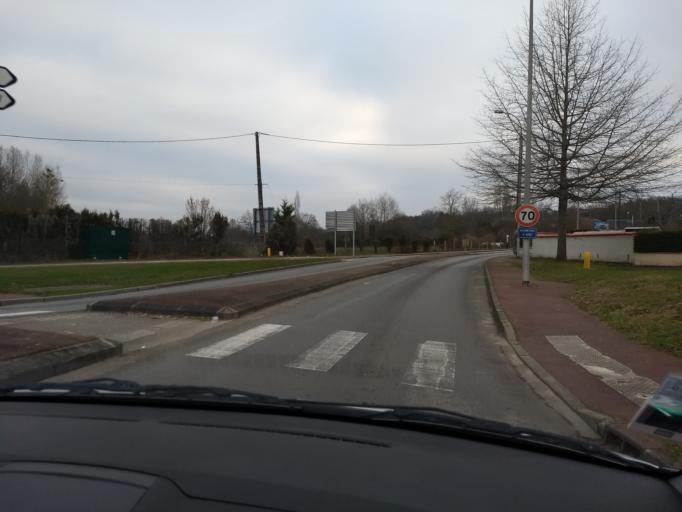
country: FR
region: Limousin
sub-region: Departement de la Haute-Vienne
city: Isle
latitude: 45.8207
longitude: 1.2088
